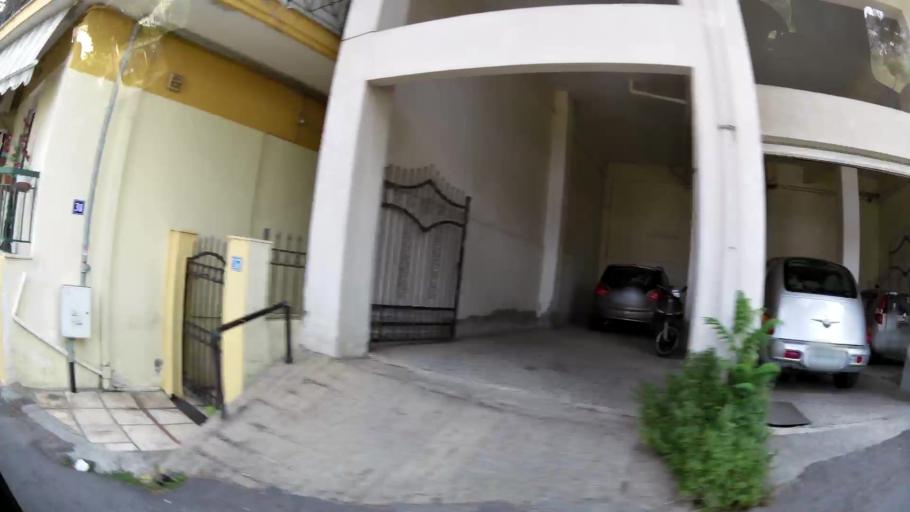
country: GR
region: Central Macedonia
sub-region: Nomos Thessalonikis
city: Sykies
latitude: 40.6573
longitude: 22.9480
